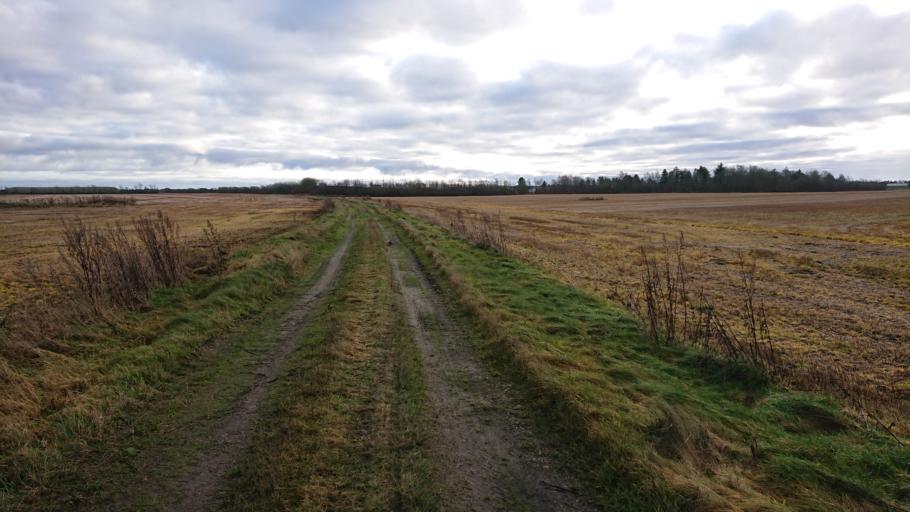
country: DK
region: Central Jutland
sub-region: Herning Kommune
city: Sunds
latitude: 56.1916
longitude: 9.0346
